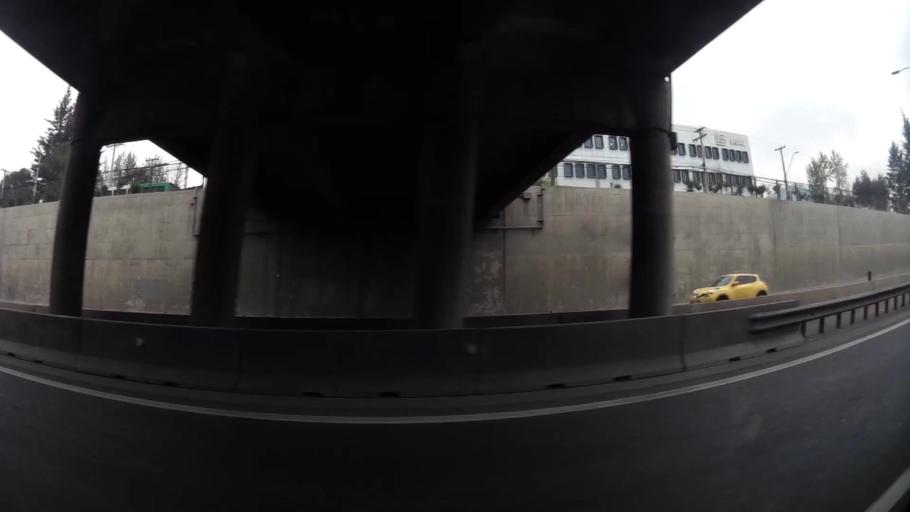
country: CL
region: Santiago Metropolitan
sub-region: Provincia de Santiago
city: Lo Prado
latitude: -33.3895
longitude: -70.6898
